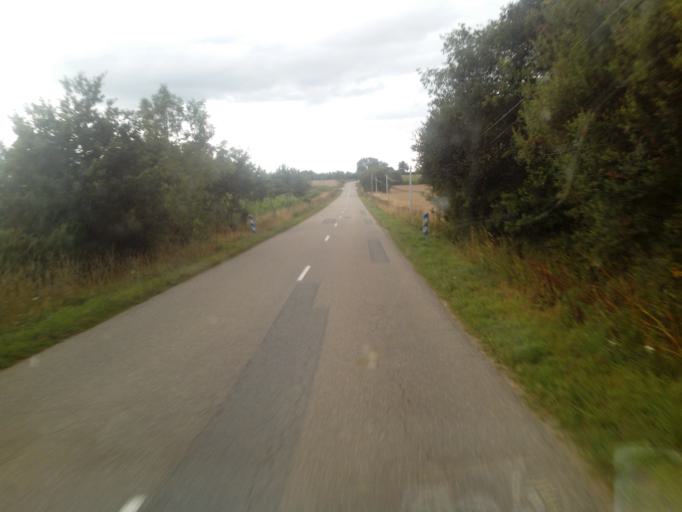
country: FR
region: Brittany
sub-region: Departement d'Ille-et-Vilaine
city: Maxent
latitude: 47.9711
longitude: -2.0198
